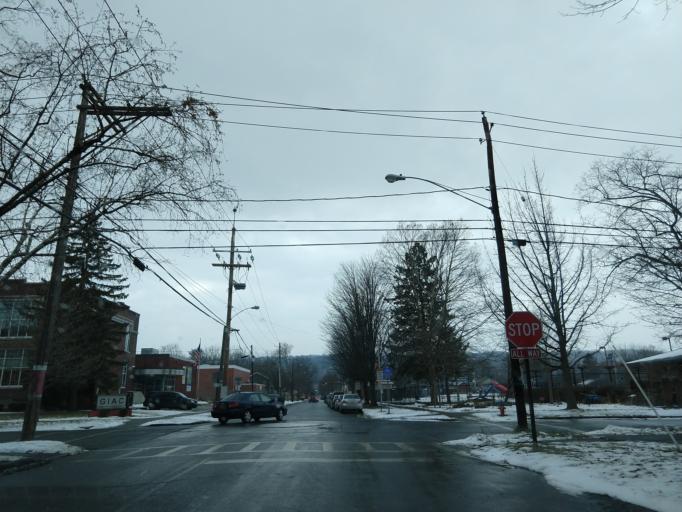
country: US
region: New York
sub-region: Tompkins County
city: Ithaca
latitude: 42.4425
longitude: -76.5017
